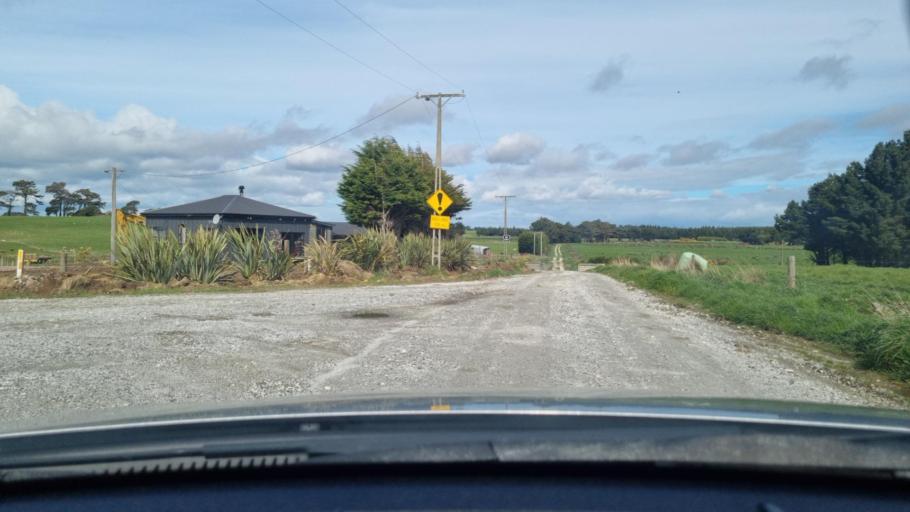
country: NZ
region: Southland
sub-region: Invercargill City
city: Invercargill
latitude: -46.4582
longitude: 168.3882
